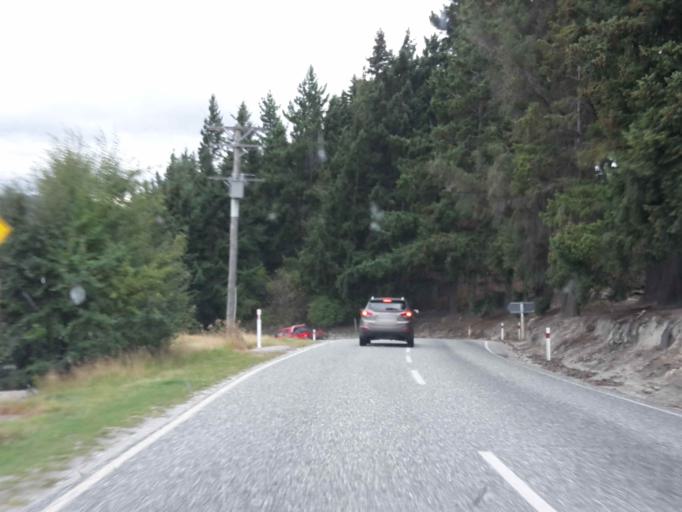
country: NZ
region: Otago
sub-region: Queenstown-Lakes District
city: Arrowtown
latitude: -44.9739
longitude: 168.8648
